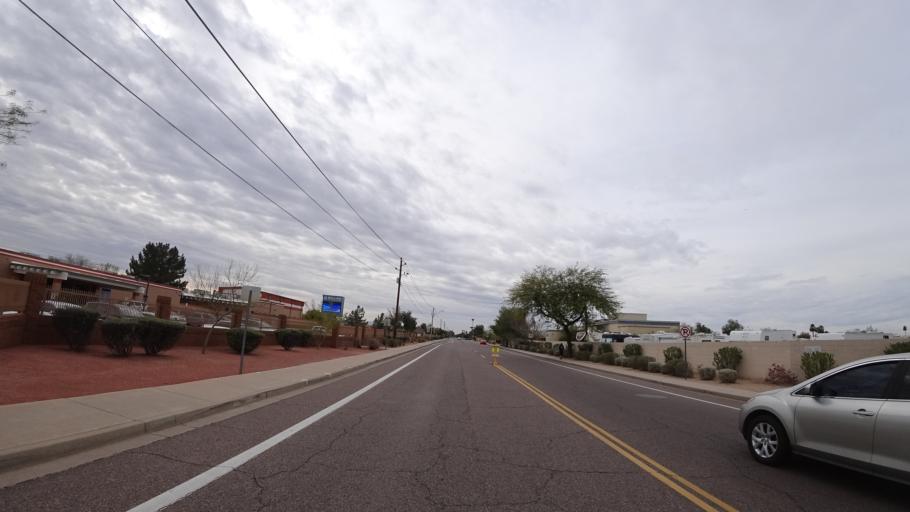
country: US
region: Arizona
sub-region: Maricopa County
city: Peoria
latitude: 33.6472
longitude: -112.1608
